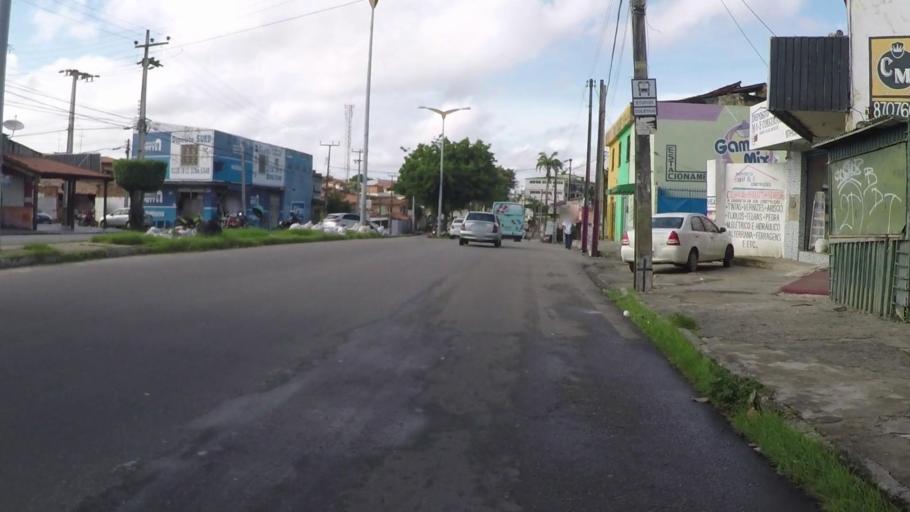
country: BR
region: Ceara
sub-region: Fortaleza
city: Fortaleza
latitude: -3.7143
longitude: -38.5889
